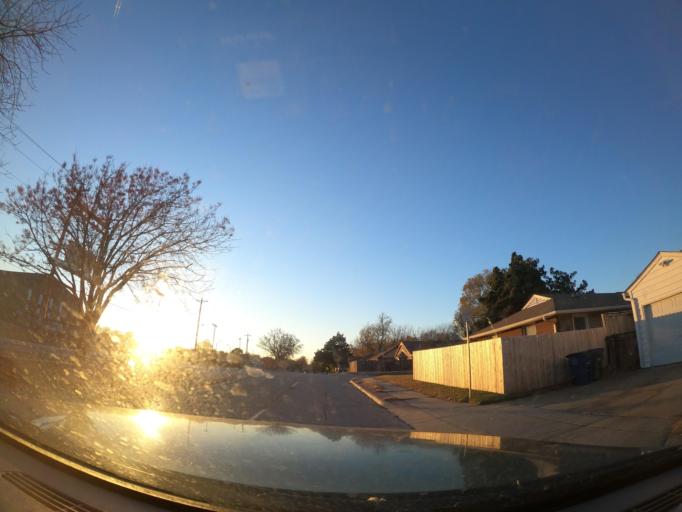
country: US
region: Oklahoma
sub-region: Tulsa County
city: Tulsa
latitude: 36.1407
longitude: -95.9323
